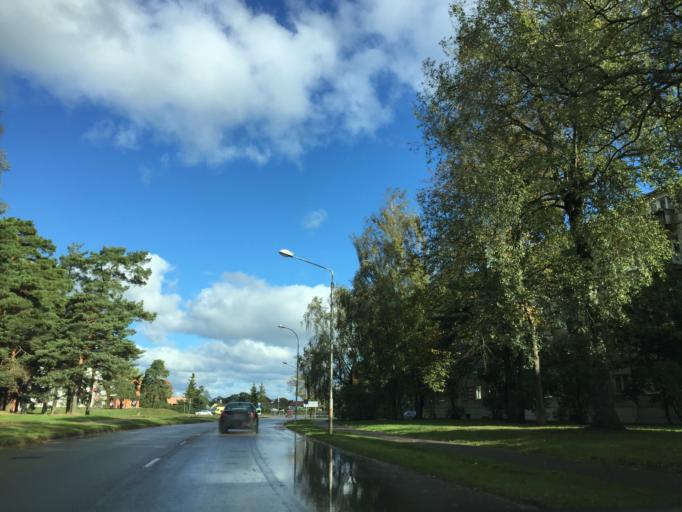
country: LV
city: Tireli
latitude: 56.9617
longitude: 23.6026
